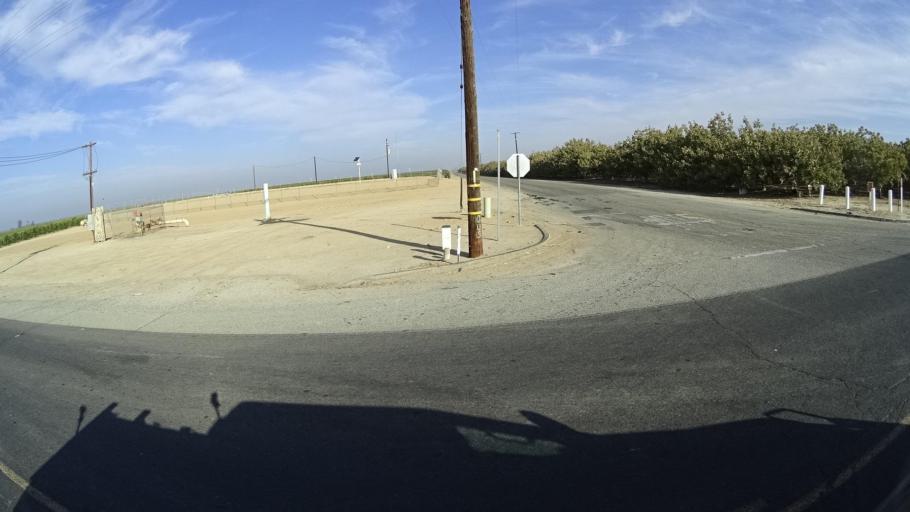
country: US
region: California
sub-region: Kern County
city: McFarland
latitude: 35.6021
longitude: -119.1691
